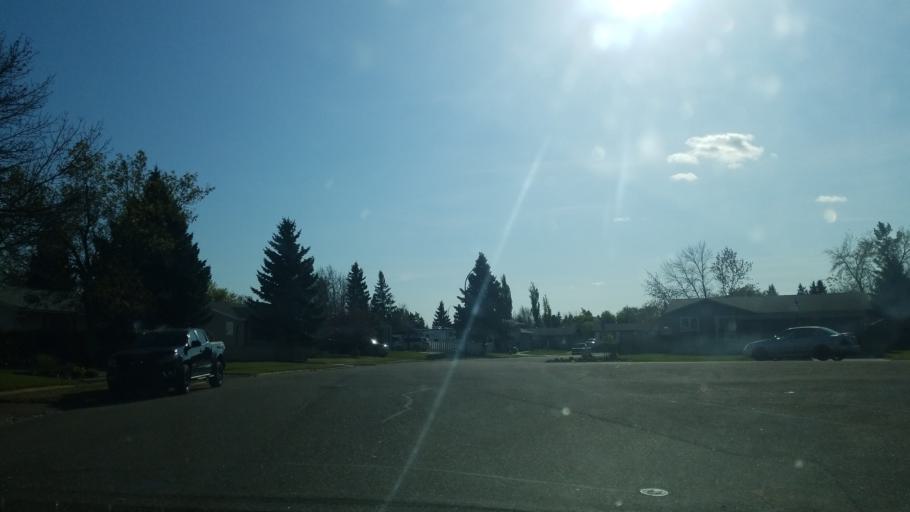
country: CA
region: Saskatchewan
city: Lloydminster
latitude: 53.2686
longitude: -110.0132
